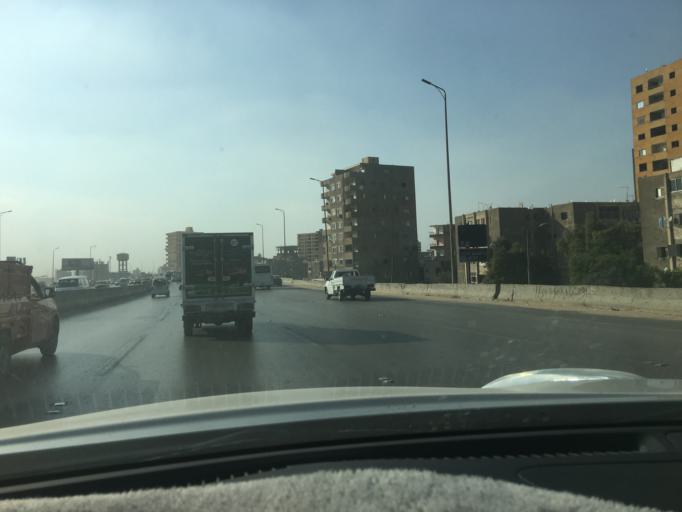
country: EG
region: Muhafazat al Qalyubiyah
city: Al Khankah
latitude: 30.1573
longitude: 31.4064
